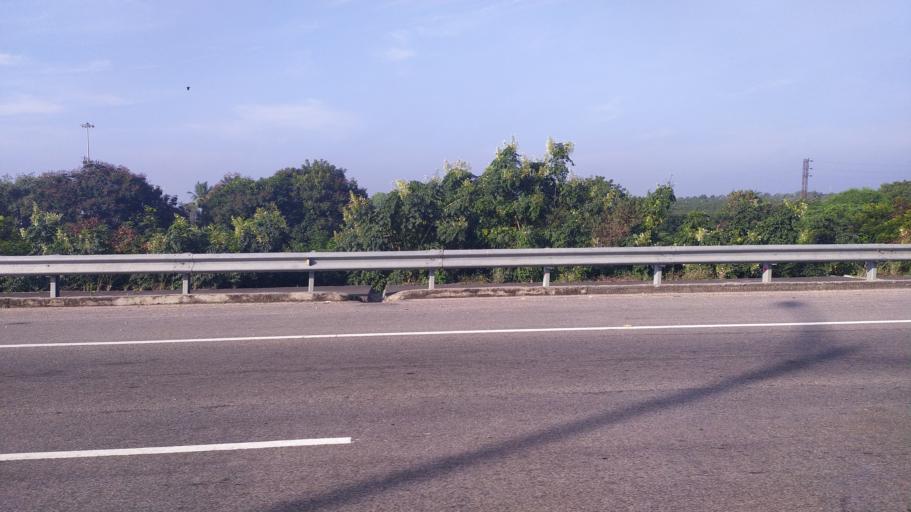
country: IN
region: Telangana
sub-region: Hyderabad
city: Hyderabad
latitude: 17.3499
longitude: 78.3599
